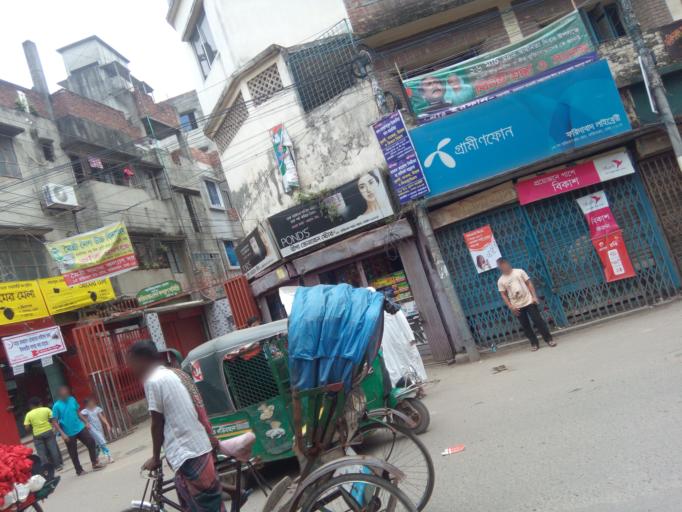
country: BD
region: Dhaka
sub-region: Dhaka
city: Dhaka
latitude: 23.6979
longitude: 90.4230
